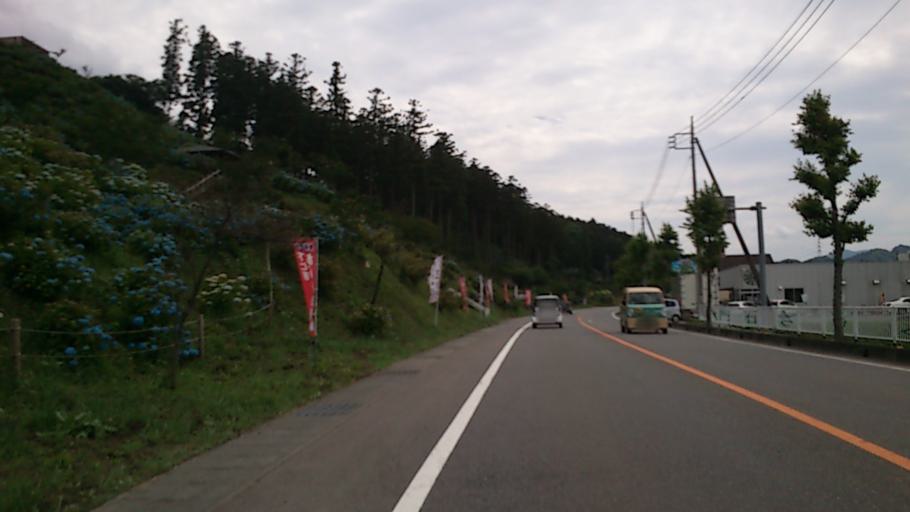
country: JP
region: Gunma
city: Tomioka
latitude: 36.2315
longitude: 138.8202
